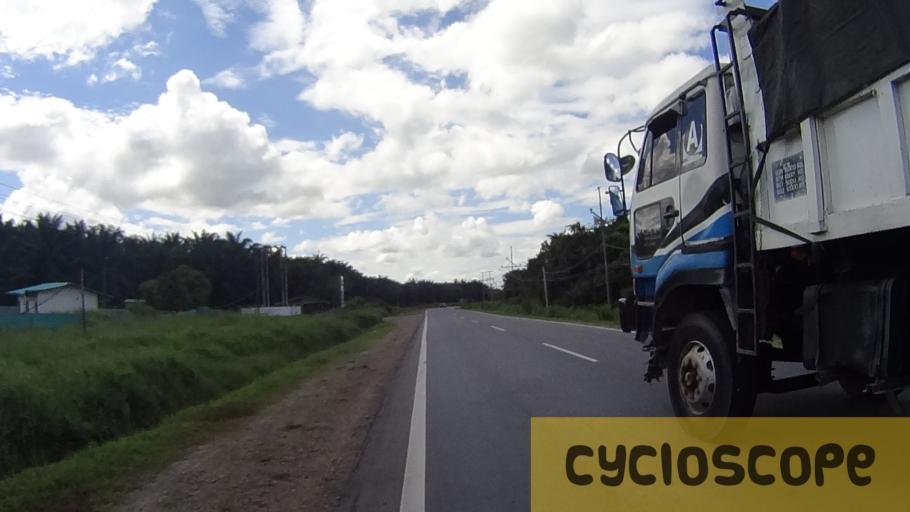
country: MY
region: Sabah
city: Beaufort
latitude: 5.3007
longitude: 115.6959
